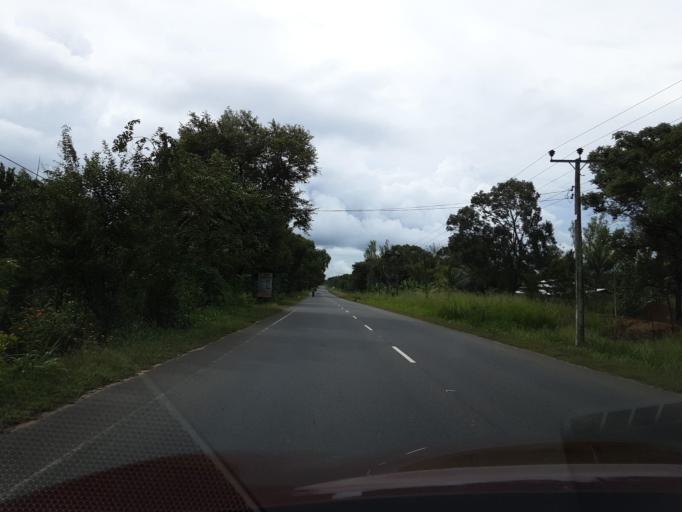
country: LK
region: Uva
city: Badulla
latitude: 7.3911
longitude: 81.1353
